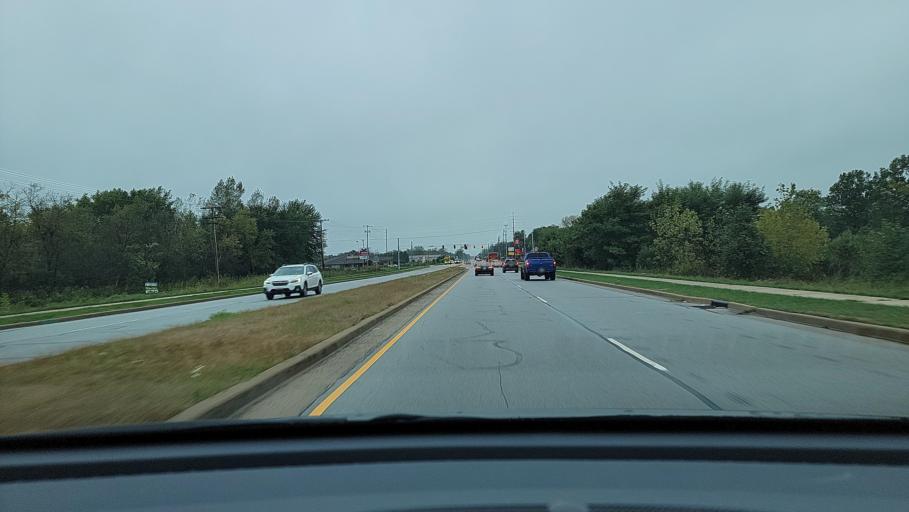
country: US
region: Indiana
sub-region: Porter County
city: Portage
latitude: 41.5506
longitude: -87.1944
